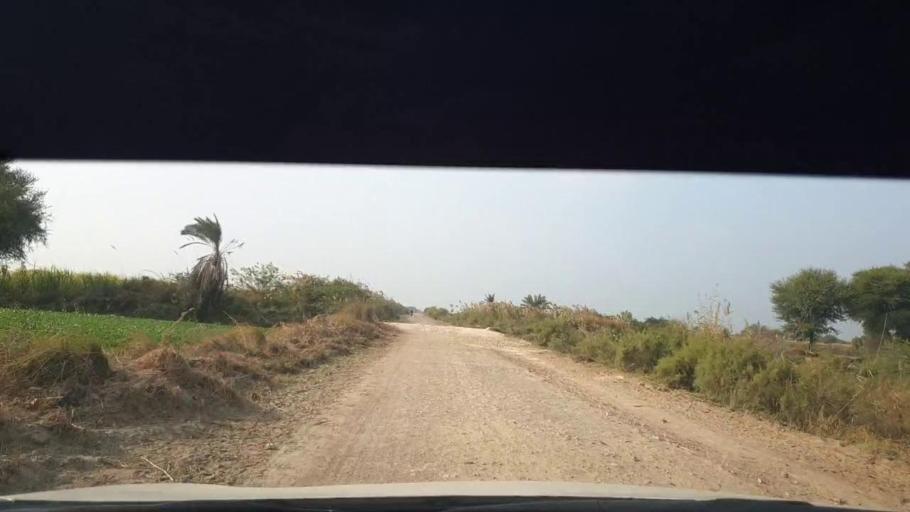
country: PK
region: Sindh
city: Berani
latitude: 25.7428
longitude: 68.9522
